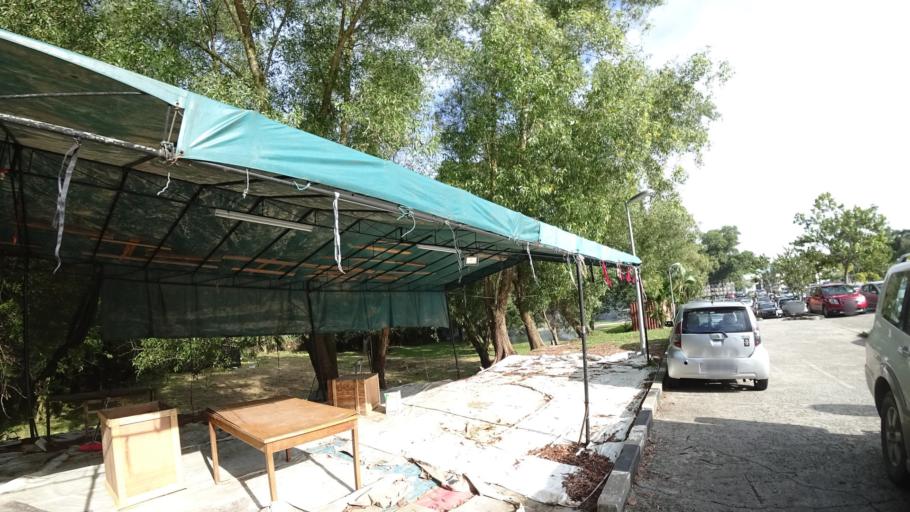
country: BN
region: Brunei and Muara
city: Bandar Seri Begawan
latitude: 4.9011
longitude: 114.9027
